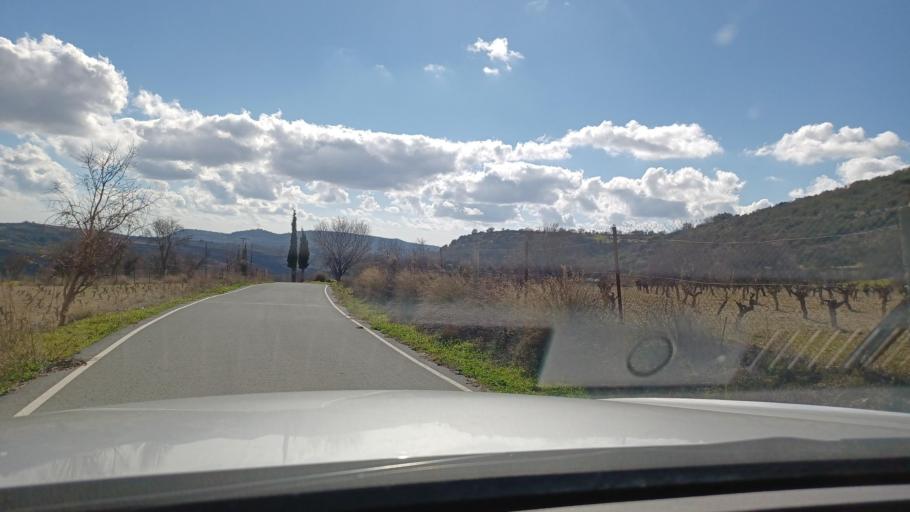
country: CY
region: Limassol
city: Pachna
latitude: 34.8288
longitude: 32.8067
